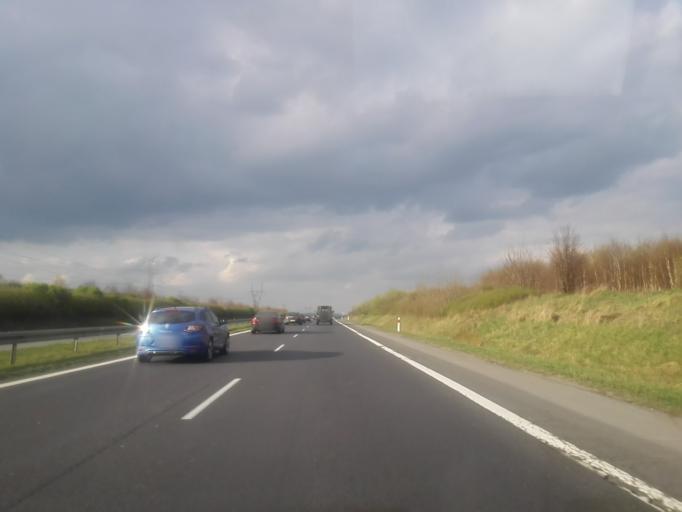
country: PL
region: Lodz Voivodeship
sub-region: Powiat radomszczanski
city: Radomsko
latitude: 51.0882
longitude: 19.3755
